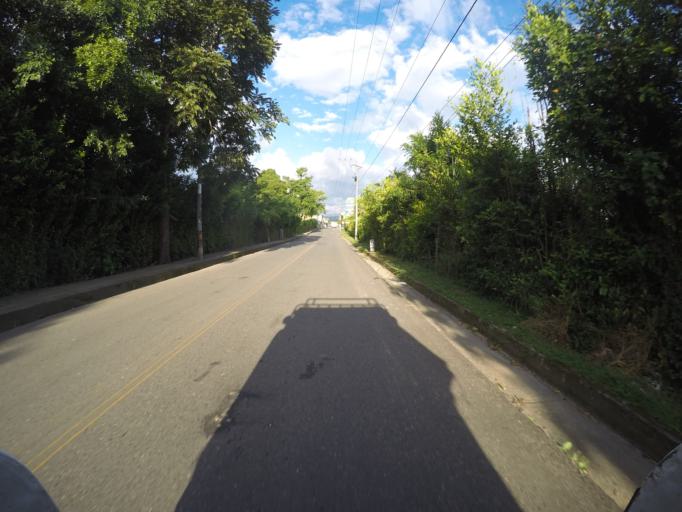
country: CO
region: Valle del Cauca
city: Alcala
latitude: 4.6763
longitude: -75.7876
